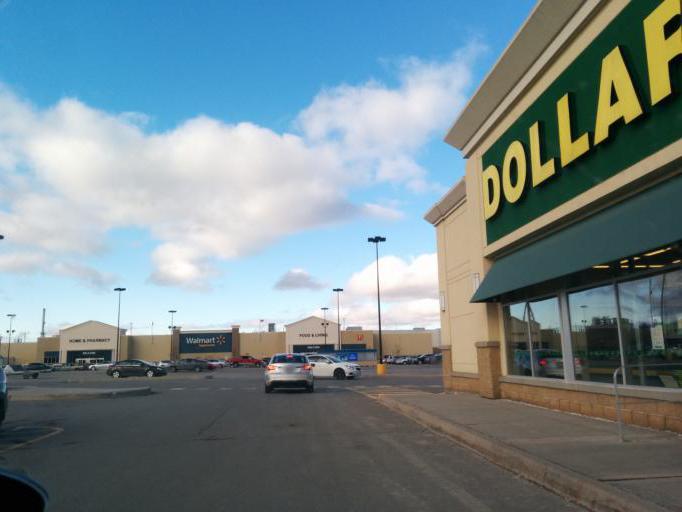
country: CA
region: Ontario
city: Bradford West Gwillimbury
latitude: 44.1082
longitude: -79.5967
